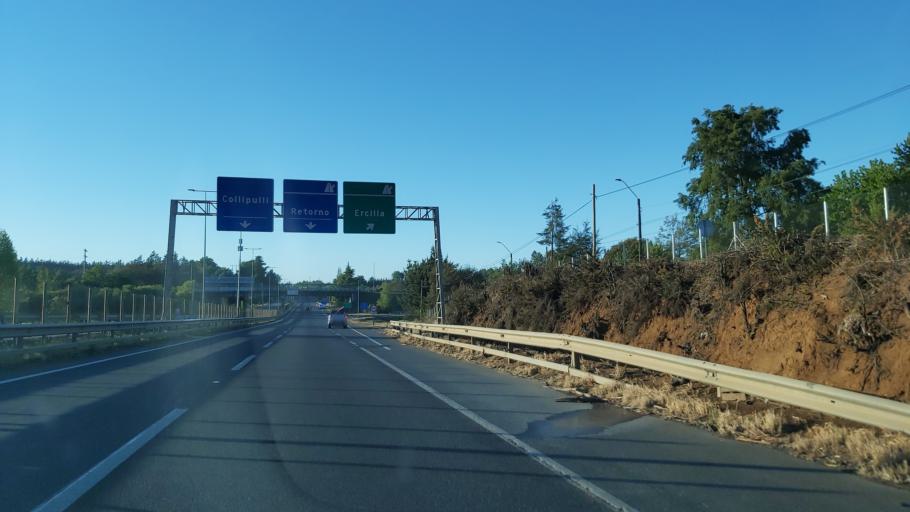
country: CL
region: Araucania
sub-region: Provincia de Malleco
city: Collipulli
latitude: -38.0674
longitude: -72.3787
